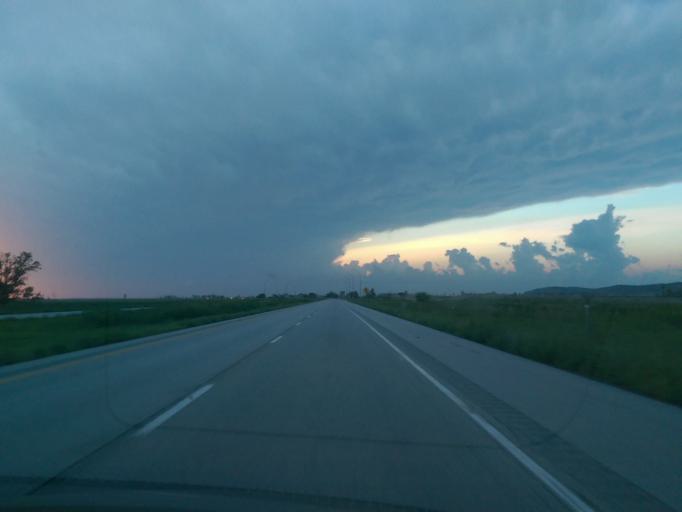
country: US
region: Iowa
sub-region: Fremont County
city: Hamburg
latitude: 40.6012
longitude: -95.6780
